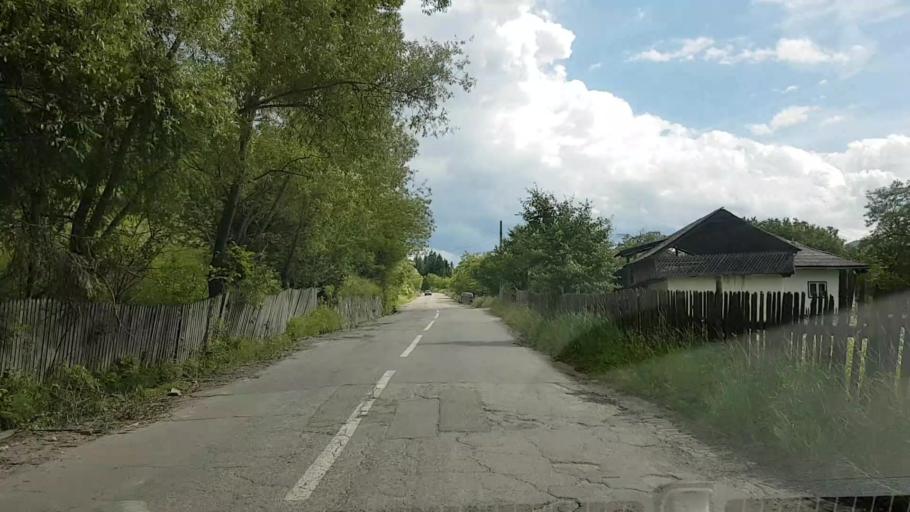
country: RO
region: Neamt
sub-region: Comuna Hangu
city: Hangu
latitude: 47.0581
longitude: 26.0373
